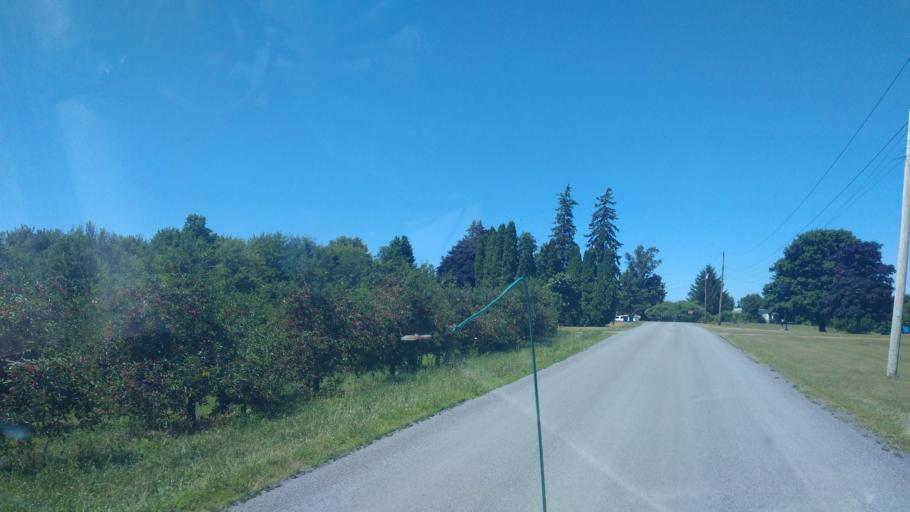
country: US
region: New York
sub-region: Wayne County
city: Lyons
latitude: 43.1660
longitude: -76.9775
